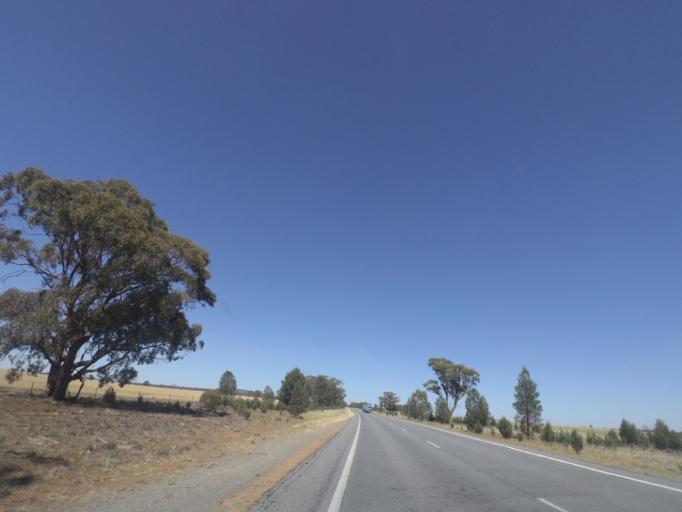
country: AU
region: New South Wales
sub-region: Narrandera
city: Narrandera
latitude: -34.4127
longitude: 146.8710
